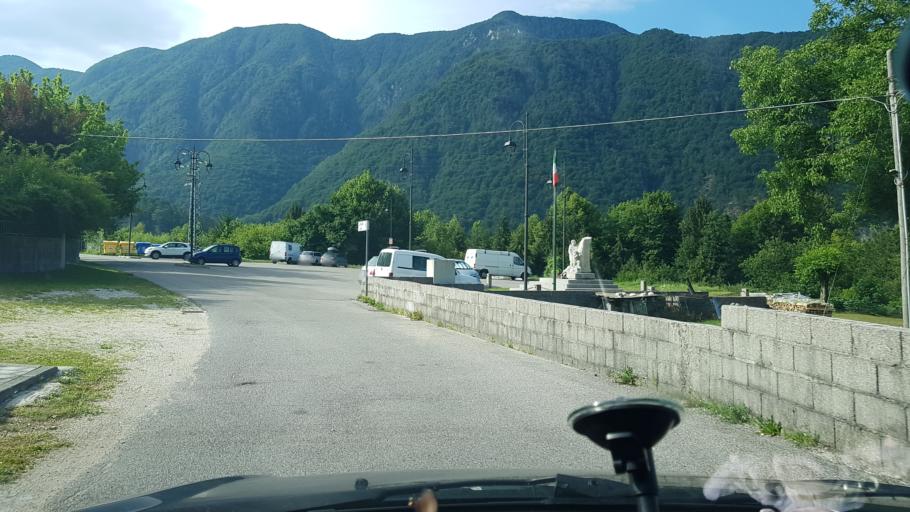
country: IT
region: Friuli Venezia Giulia
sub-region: Provincia di Udine
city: Prato
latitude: 46.3613
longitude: 13.3542
